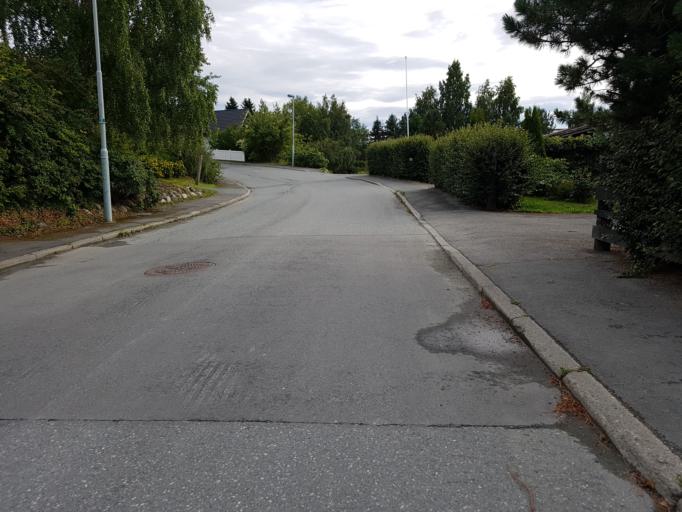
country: NO
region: Sor-Trondelag
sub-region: Trondheim
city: Trondheim
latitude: 63.4024
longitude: 10.4324
